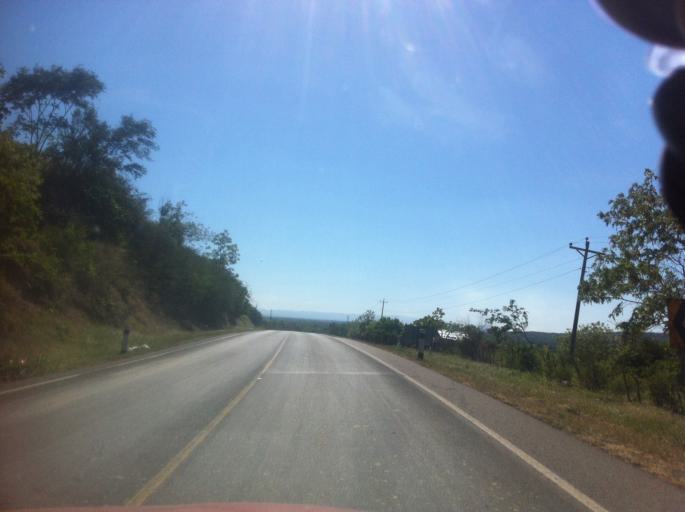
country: NI
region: Boaco
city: Teustepe
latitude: 12.3558
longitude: -85.9218
